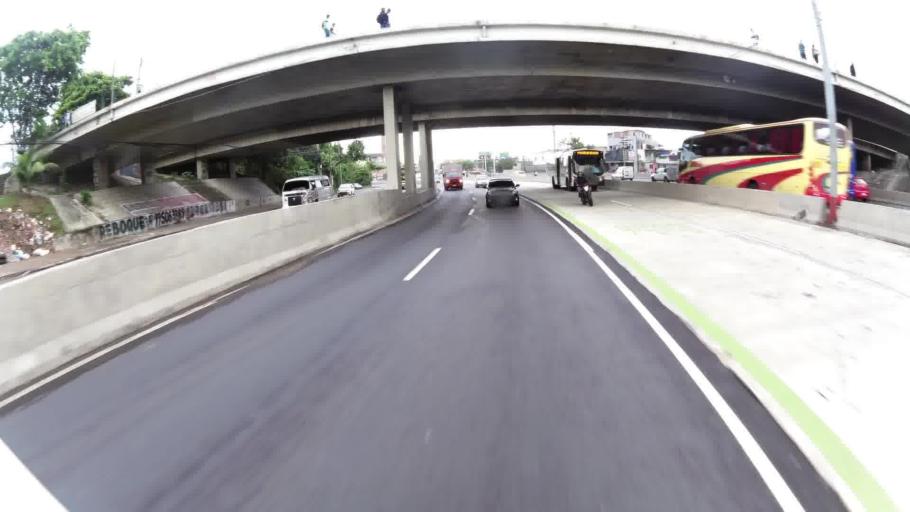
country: BR
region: Rio de Janeiro
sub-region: Rio De Janeiro
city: Rio de Janeiro
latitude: -22.8870
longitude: -43.2329
